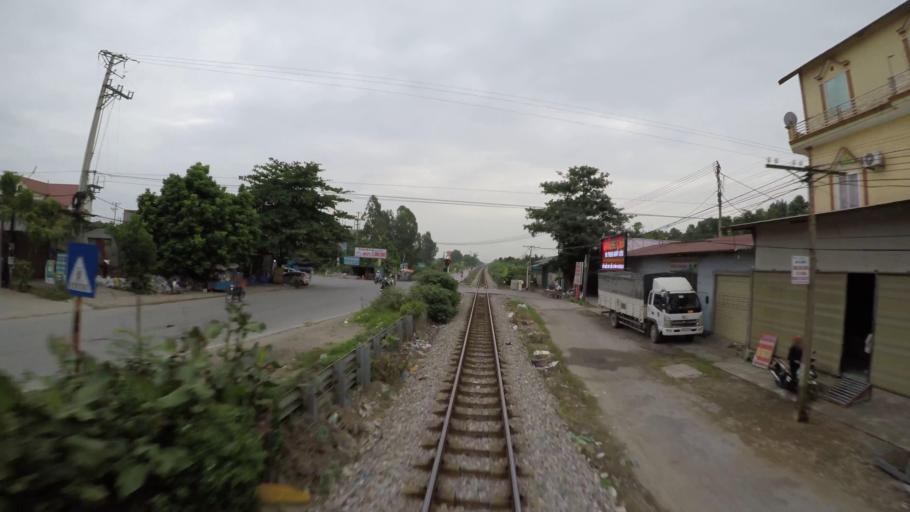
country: VN
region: Hung Yen
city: Ban Yen Nhan
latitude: 20.9853
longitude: 106.0591
